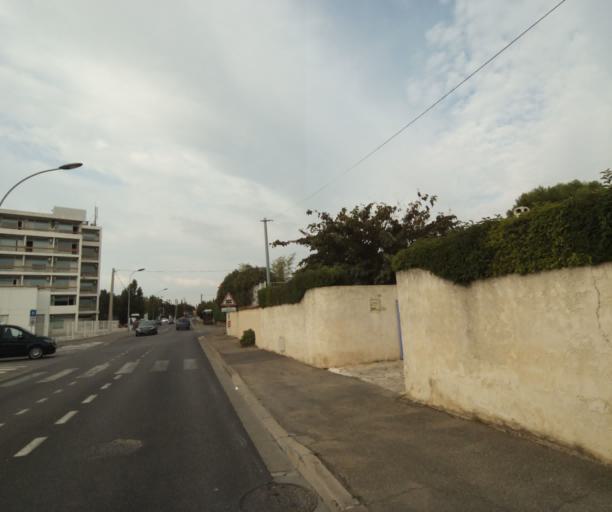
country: FR
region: Provence-Alpes-Cote d'Azur
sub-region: Departement des Bouches-du-Rhone
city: Marignane
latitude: 43.4088
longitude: 5.2151
